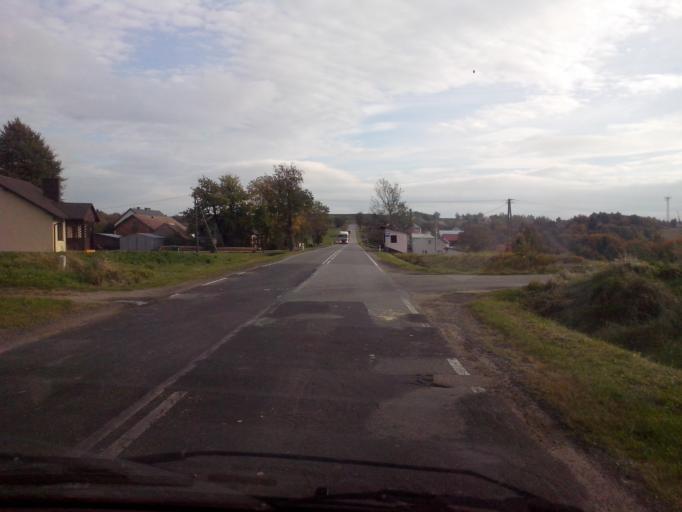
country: PL
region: Subcarpathian Voivodeship
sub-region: Powiat ropczycko-sedziszowski
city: Wielopole Skrzynskie
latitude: 49.9228
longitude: 21.6104
